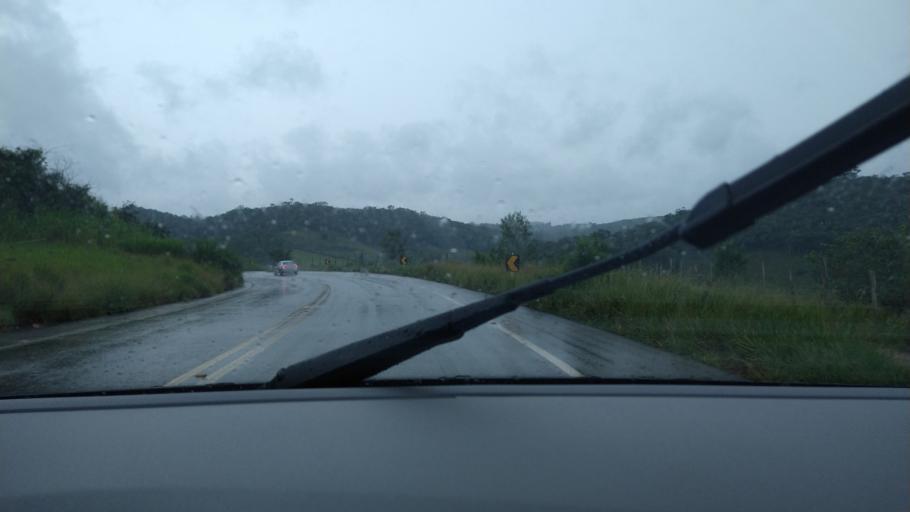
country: BR
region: Minas Gerais
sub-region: Vicosa
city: Vicosa
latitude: -20.6068
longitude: -42.8666
